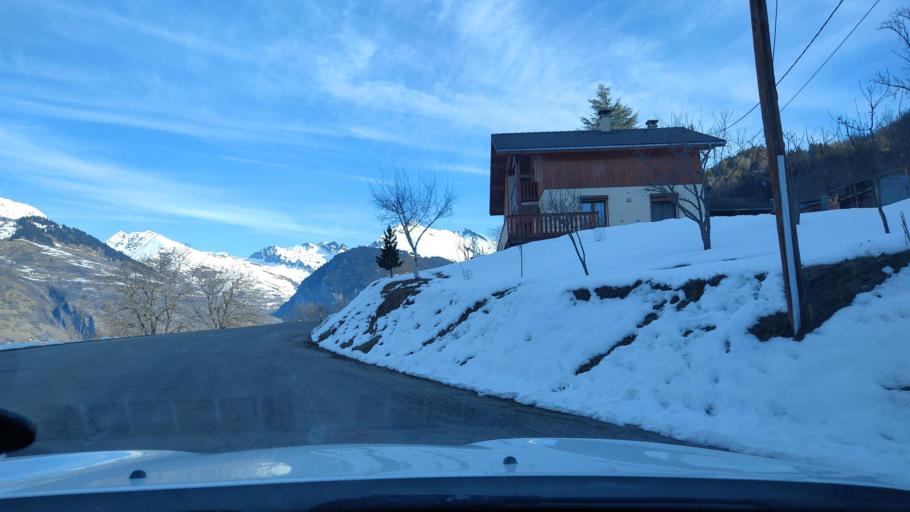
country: FR
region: Rhone-Alpes
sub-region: Departement de la Savoie
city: Bourg-Saint-Maurice
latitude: 45.5942
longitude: 6.7616
